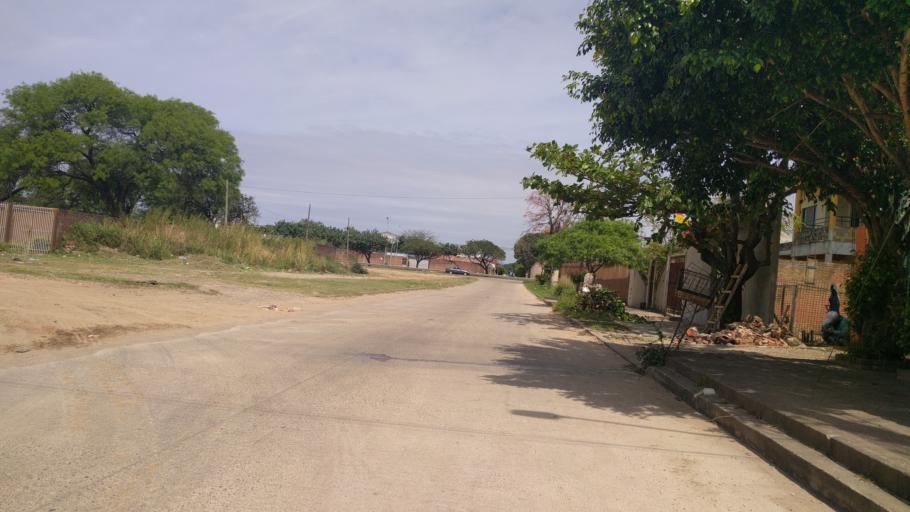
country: BO
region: Santa Cruz
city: Santa Cruz de la Sierra
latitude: -17.8199
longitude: -63.2211
